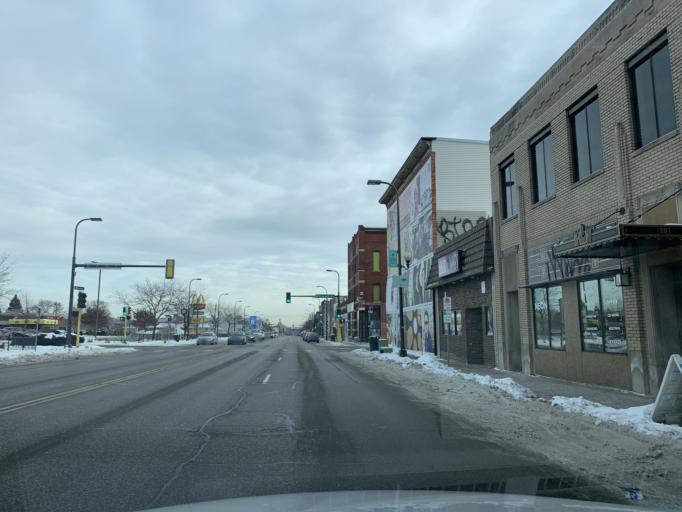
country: US
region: Minnesota
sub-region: Hennepin County
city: Minneapolis
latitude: 44.9991
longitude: -93.2933
